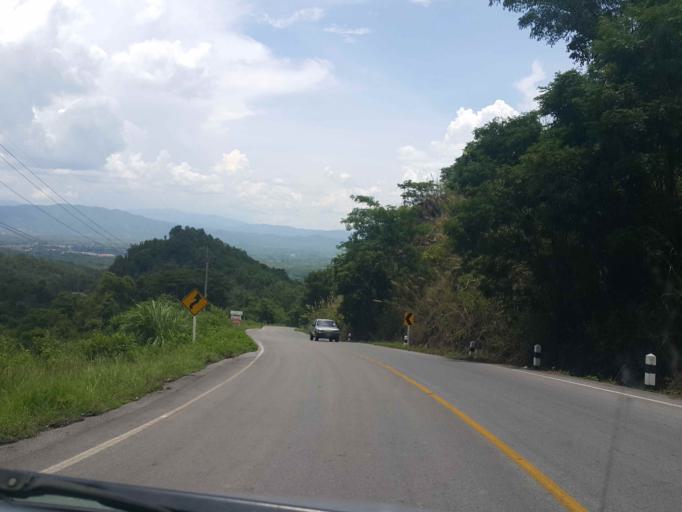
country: TH
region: Phayao
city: Chiang Muan
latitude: 18.9204
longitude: 100.1972
